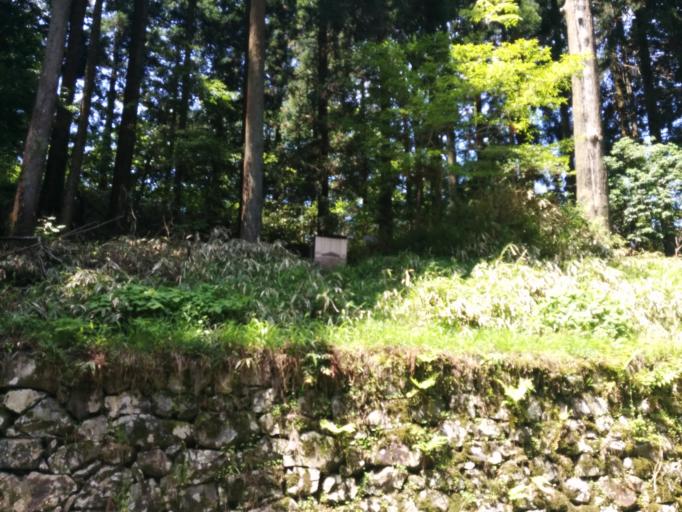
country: JP
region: Shiga Prefecture
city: Otsu-shi
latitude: 35.0742
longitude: 135.8338
